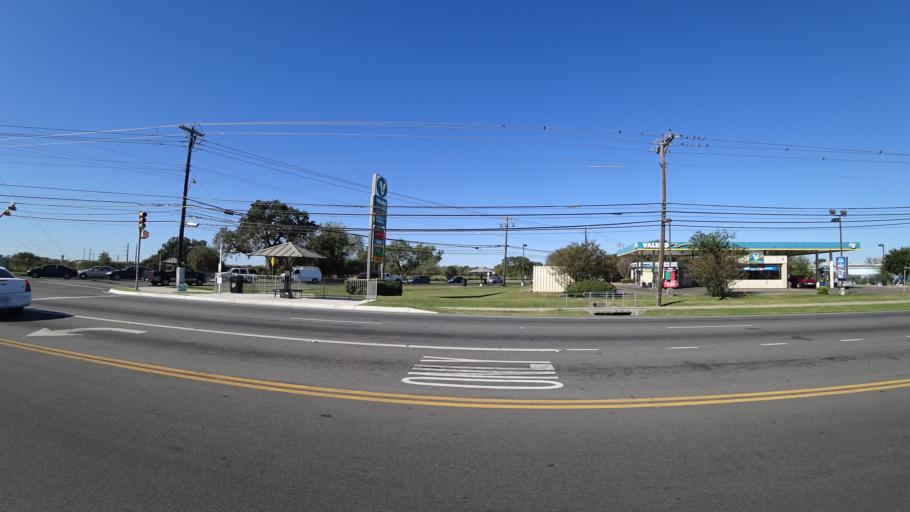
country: US
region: Texas
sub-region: Travis County
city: Austin
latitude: 30.2858
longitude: -97.6822
